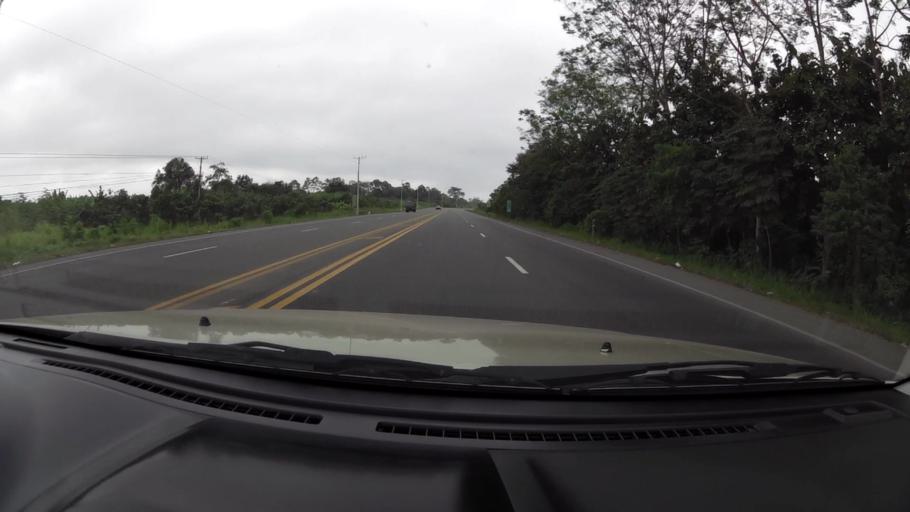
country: EC
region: Guayas
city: Naranjal
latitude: -2.5596
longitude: -79.5577
